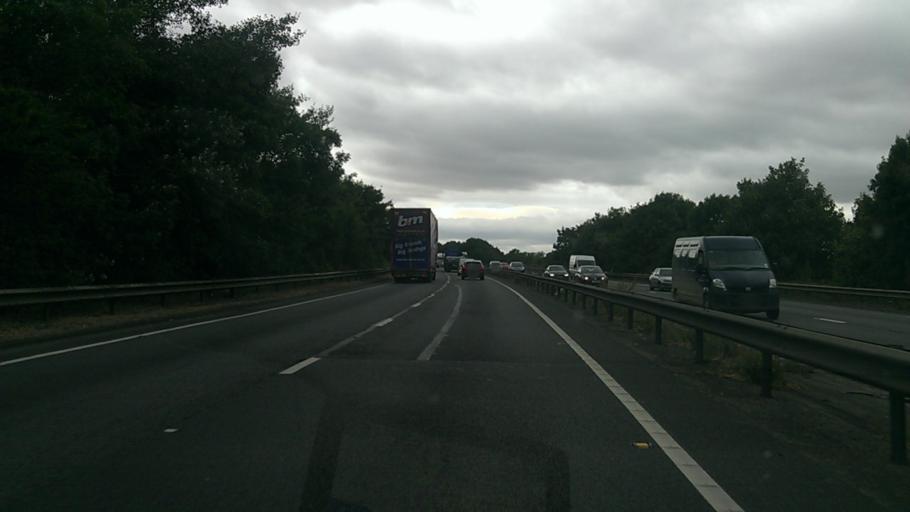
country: GB
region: England
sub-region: Cambridgeshire
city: Godmanchester
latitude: 52.3243
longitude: -0.1727
